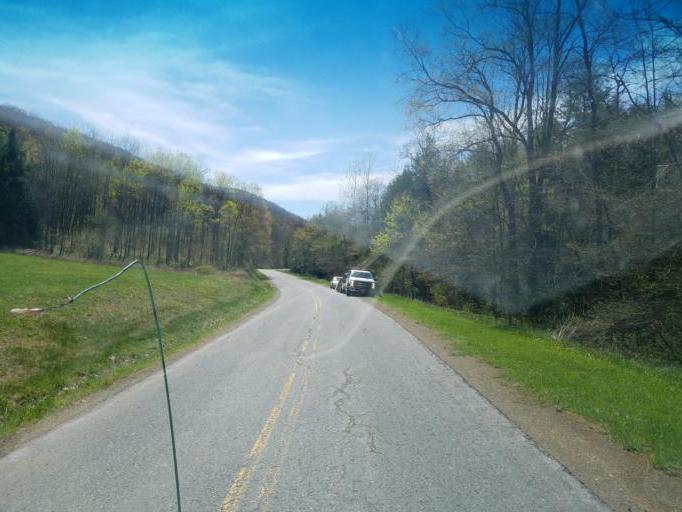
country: US
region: Pennsylvania
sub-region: Potter County
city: Galeton
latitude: 41.8659
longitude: -77.7195
